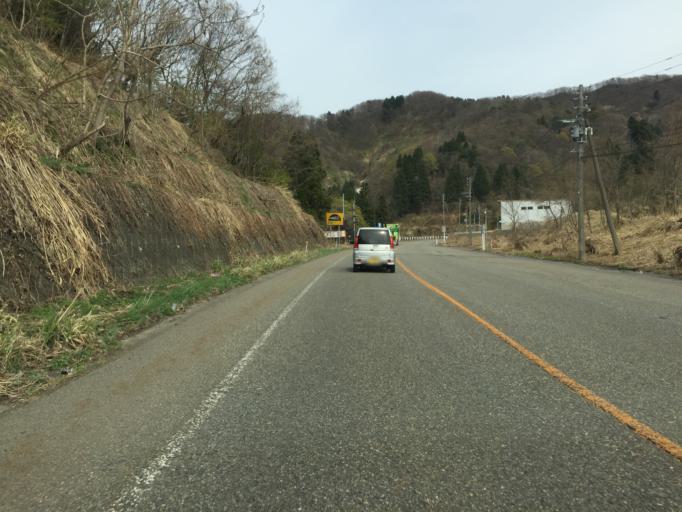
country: JP
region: Niigata
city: Nagaoka
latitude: 37.4558
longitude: 138.9199
